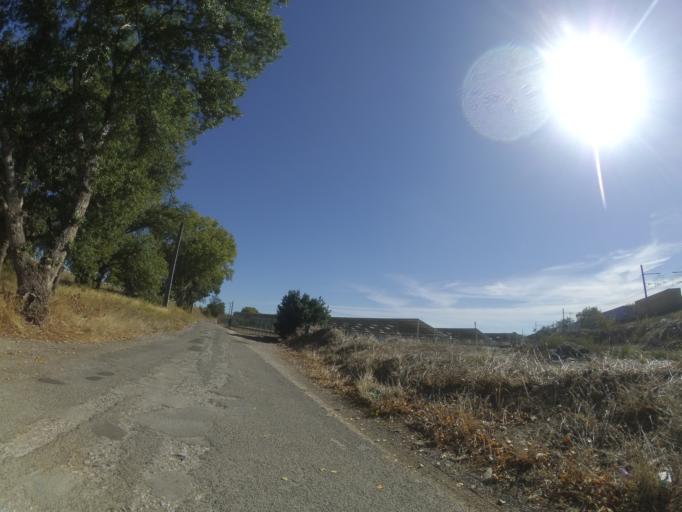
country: FR
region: Languedoc-Roussillon
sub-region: Departement des Pyrenees-Orientales
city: Perpignan
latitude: 42.7099
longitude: 2.8739
